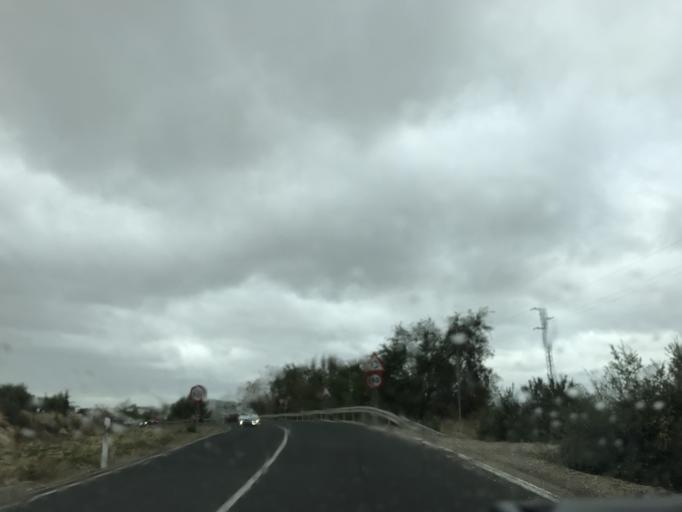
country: ES
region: Andalusia
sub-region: Provincia de Jaen
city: Peal de Becerro
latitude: 37.9199
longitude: -3.1189
